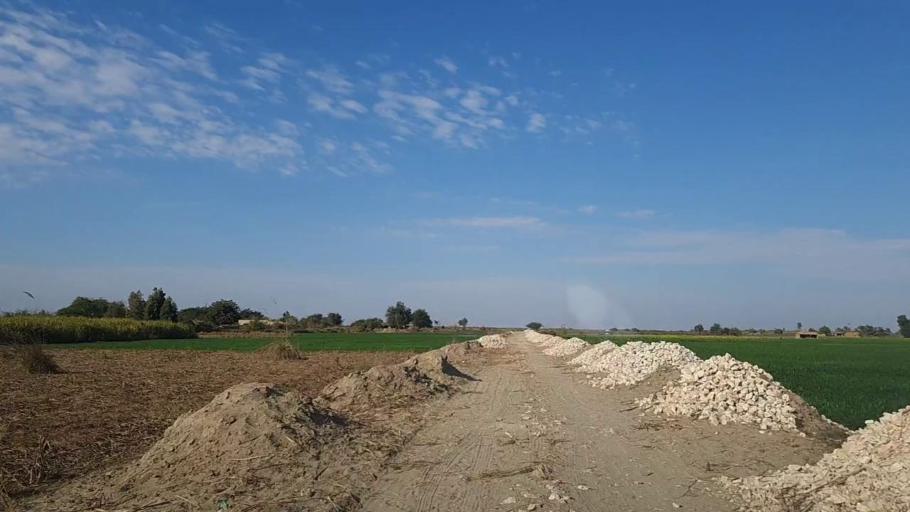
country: PK
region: Sindh
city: Jam Sahib
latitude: 26.3144
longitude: 68.8081
